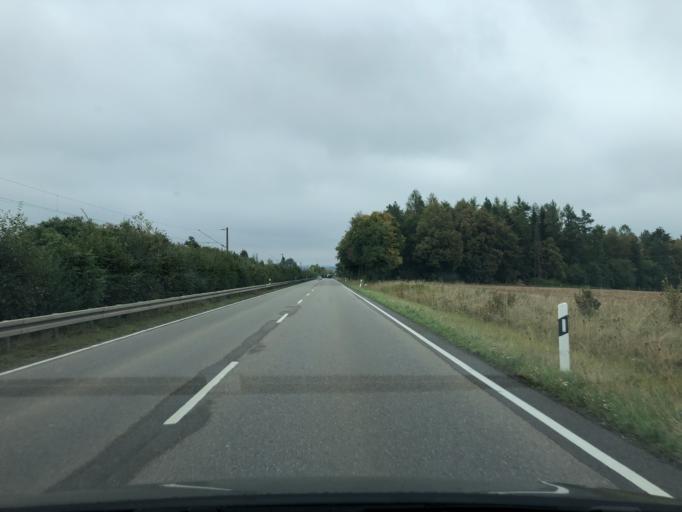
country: DE
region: Baden-Wuerttemberg
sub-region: Regierungsbezirk Stuttgart
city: Herrenberg
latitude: 48.5665
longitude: 8.8548
